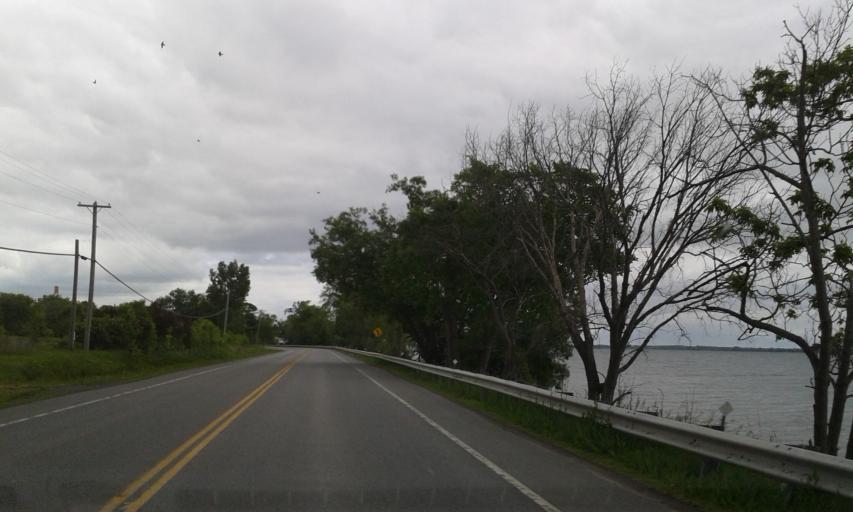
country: CA
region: Ontario
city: Skatepark
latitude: 44.1591
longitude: -76.8146
